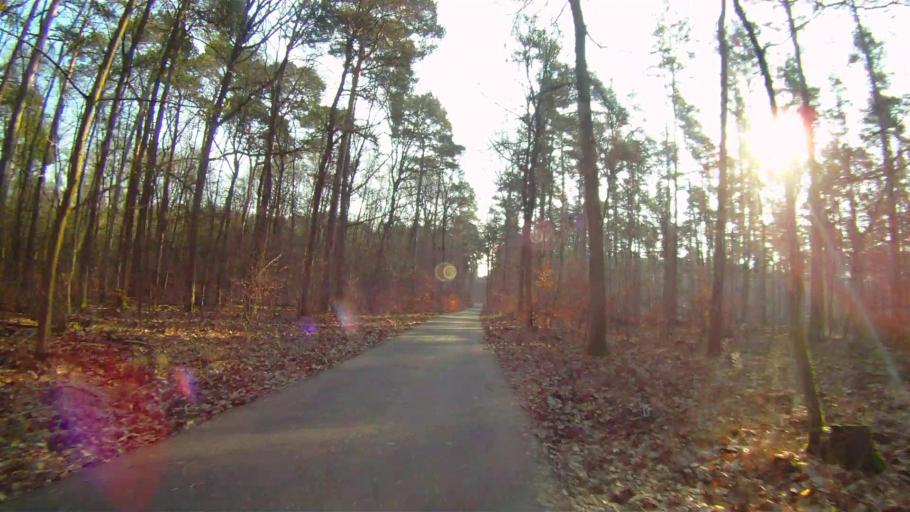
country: DE
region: Berlin
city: Rahnsdorf
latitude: 52.4198
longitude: 13.7108
